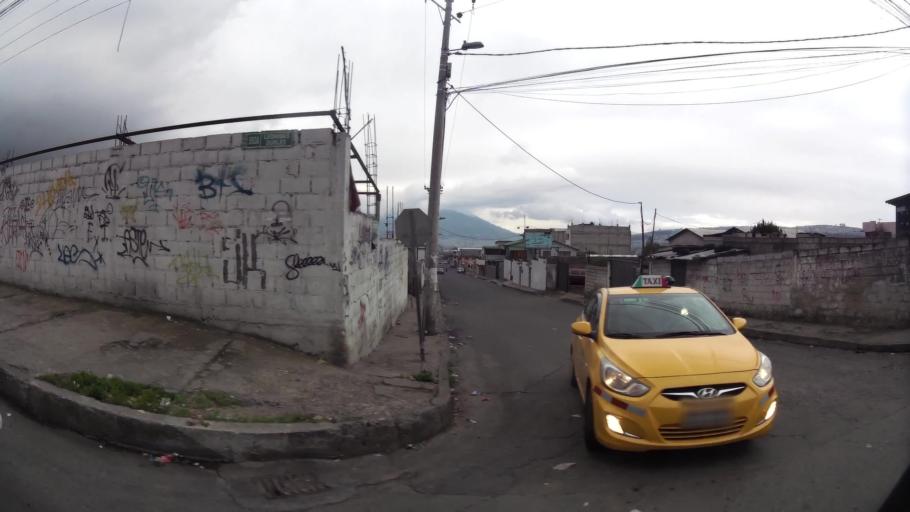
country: EC
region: Pichincha
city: Sangolqui
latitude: -0.3276
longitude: -78.5497
